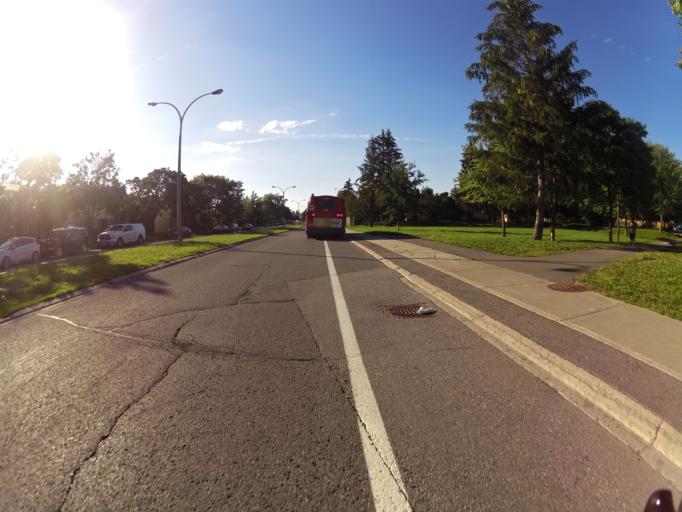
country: CA
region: Ontario
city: Bells Corners
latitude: 45.3329
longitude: -75.7562
